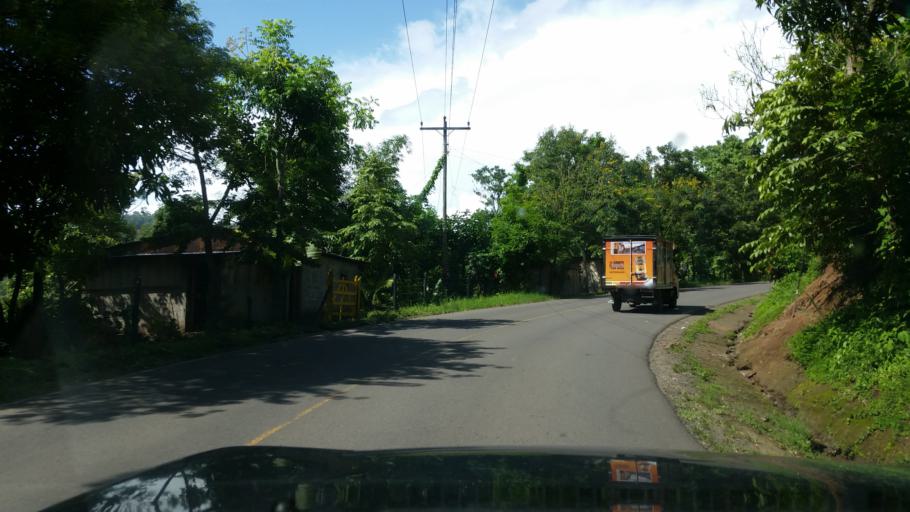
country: NI
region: Matagalpa
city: San Ramon
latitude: 13.0060
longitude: -85.8117
